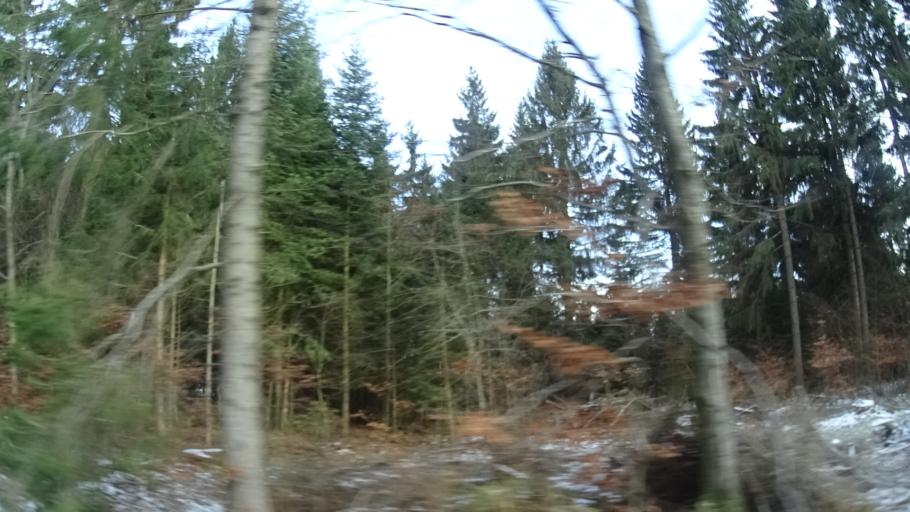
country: DE
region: Thuringia
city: Tabarz
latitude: 50.8346
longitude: 10.5183
